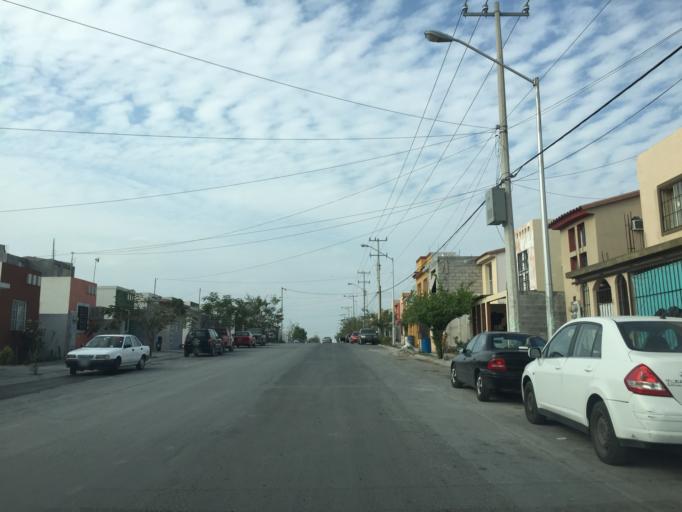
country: MX
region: Nuevo Leon
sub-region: Apodaca
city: Fraccionamiento Cosmopolis Octavo Sector
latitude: 25.8211
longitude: -100.2569
